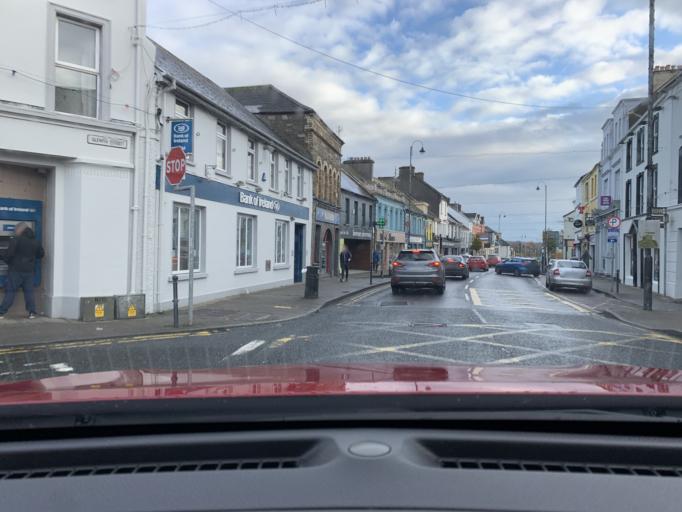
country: IE
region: Ulster
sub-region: County Donegal
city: Ballybofey
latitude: 54.7993
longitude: -7.7829
